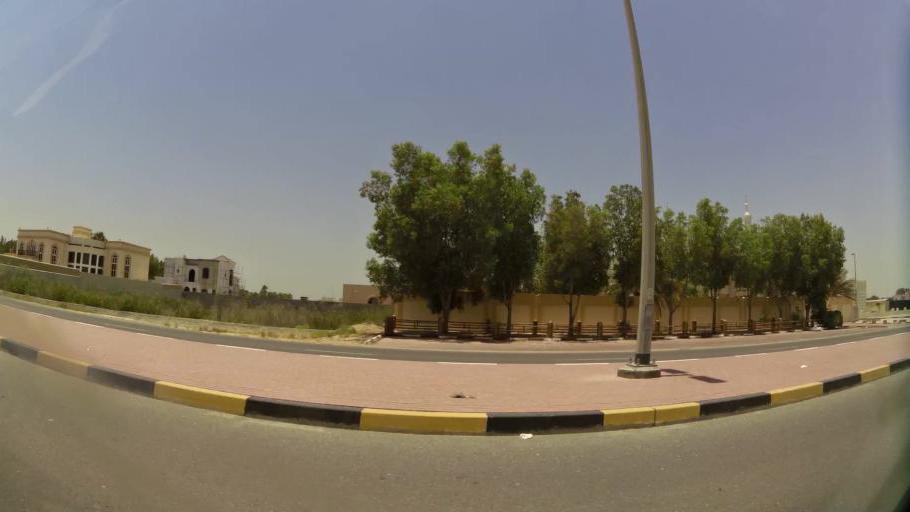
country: AE
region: Ajman
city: Ajman
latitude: 25.4150
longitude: 55.4901
